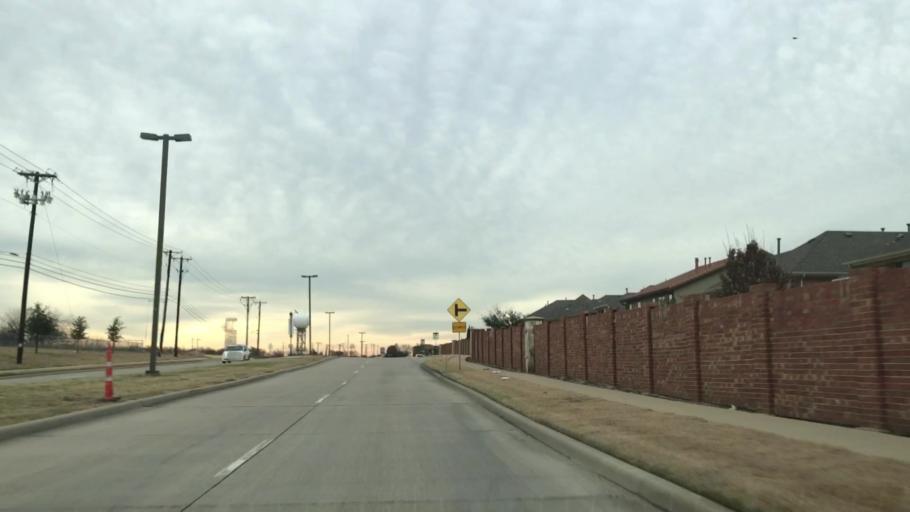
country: US
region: Texas
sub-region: Dallas County
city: Coppell
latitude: 32.9254
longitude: -96.9746
